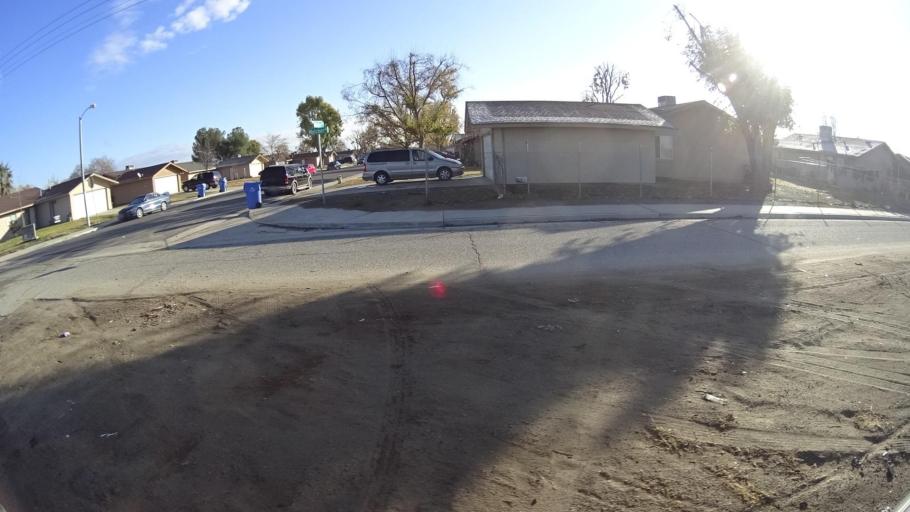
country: US
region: California
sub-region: Kern County
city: Delano
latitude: 35.7706
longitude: -119.2763
